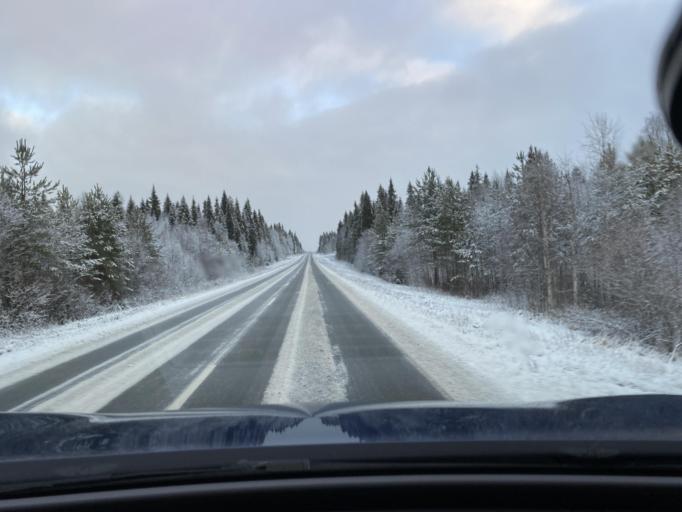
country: FI
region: Lapland
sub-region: Rovaniemi
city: Ranua
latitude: 65.9724
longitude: 26.1057
